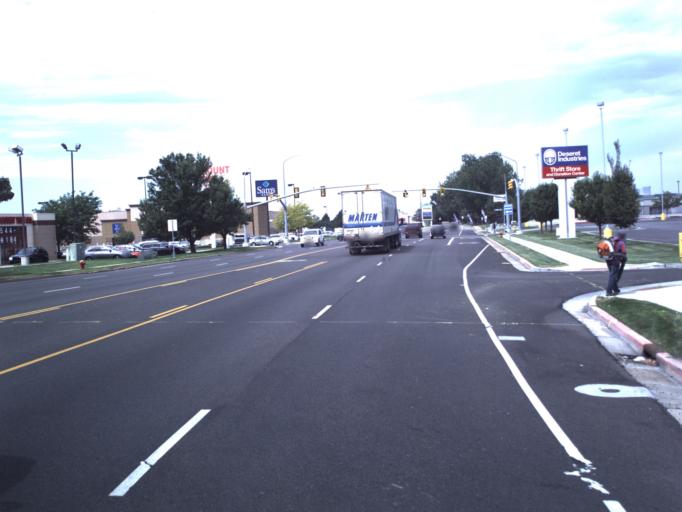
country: US
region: Utah
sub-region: Davis County
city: Layton
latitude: 41.0720
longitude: -111.9811
